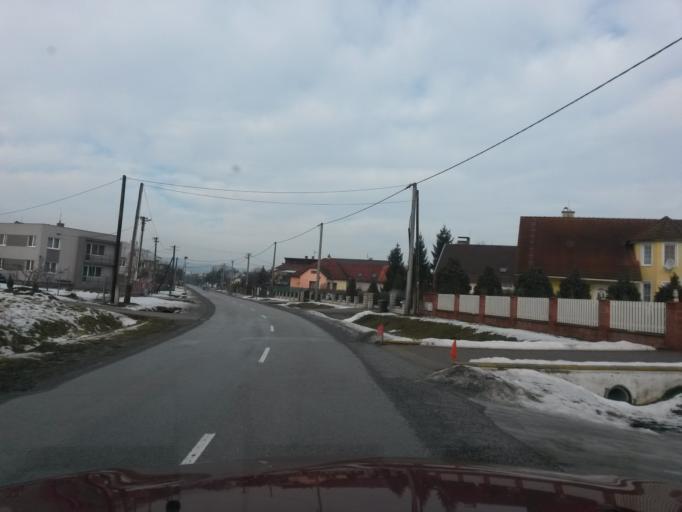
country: SK
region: Kosicky
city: Kosice
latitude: 48.7808
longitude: 21.3288
